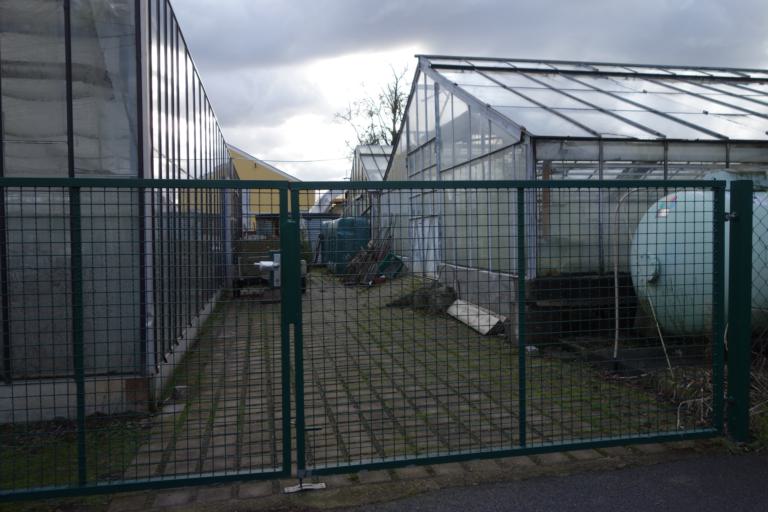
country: DE
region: Saxony
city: Radebeul
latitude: 51.0547
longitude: 13.6573
